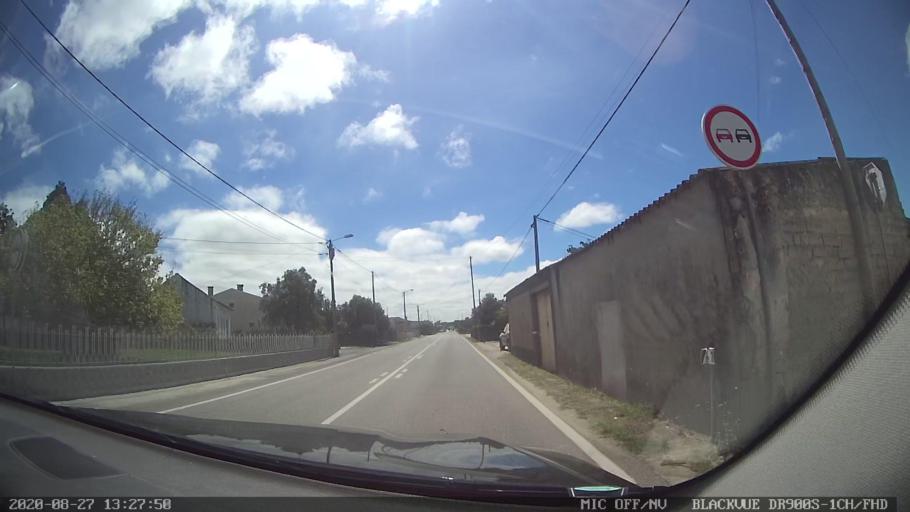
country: PT
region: Aveiro
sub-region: Vagos
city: Vagos
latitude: 40.5266
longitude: -8.6792
